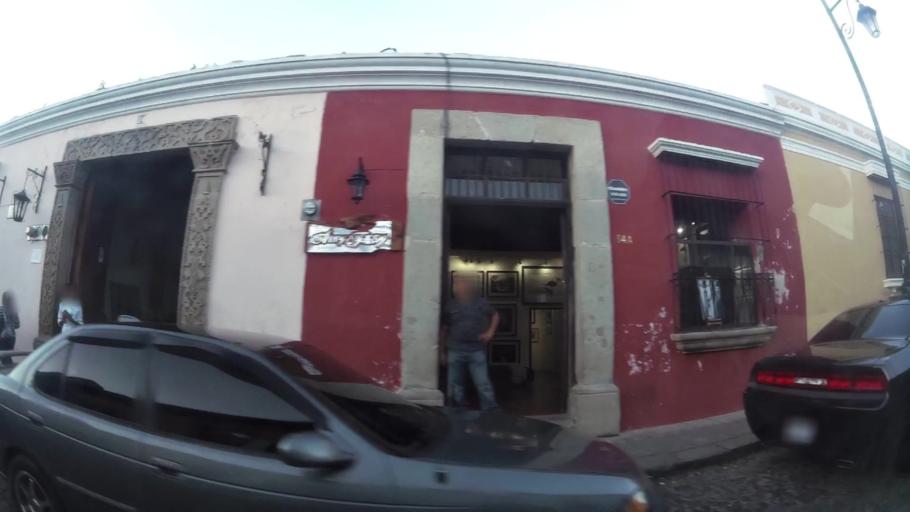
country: GT
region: Sacatepequez
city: Antigua Guatemala
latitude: 14.5574
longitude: -90.7316
